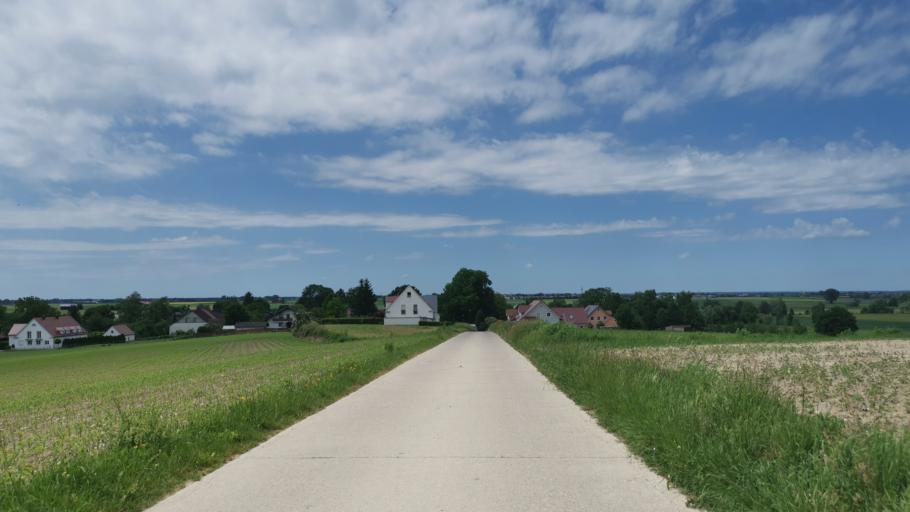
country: DE
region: Bavaria
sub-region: Swabia
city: Steindorf
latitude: 48.2383
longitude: 11.0222
